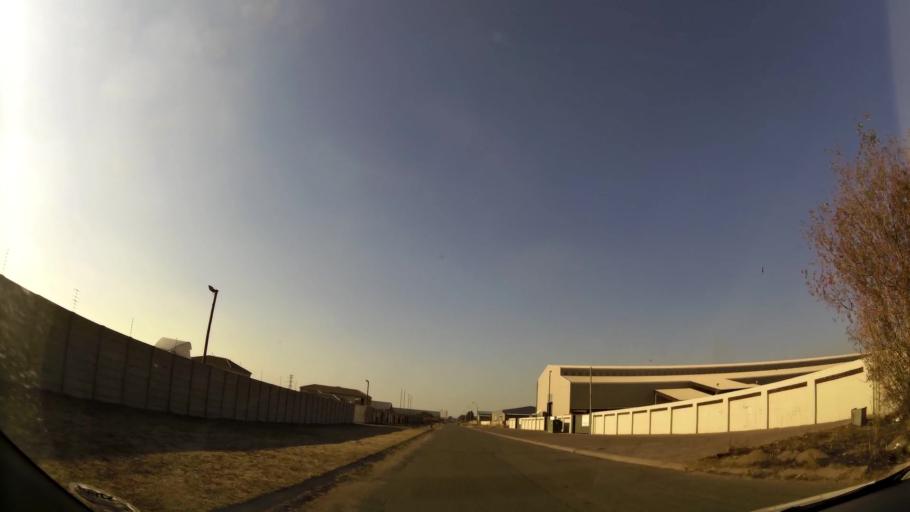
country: ZA
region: Gauteng
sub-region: West Rand District Municipality
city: Randfontein
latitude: -26.1963
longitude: 27.6915
